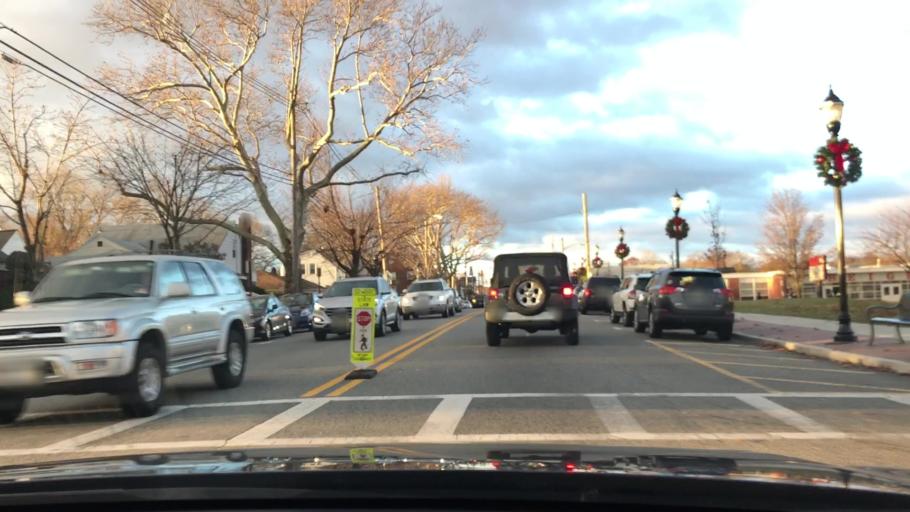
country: US
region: New Jersey
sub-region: Bergen County
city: Hasbrouck Heights
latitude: 40.8673
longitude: -74.0728
